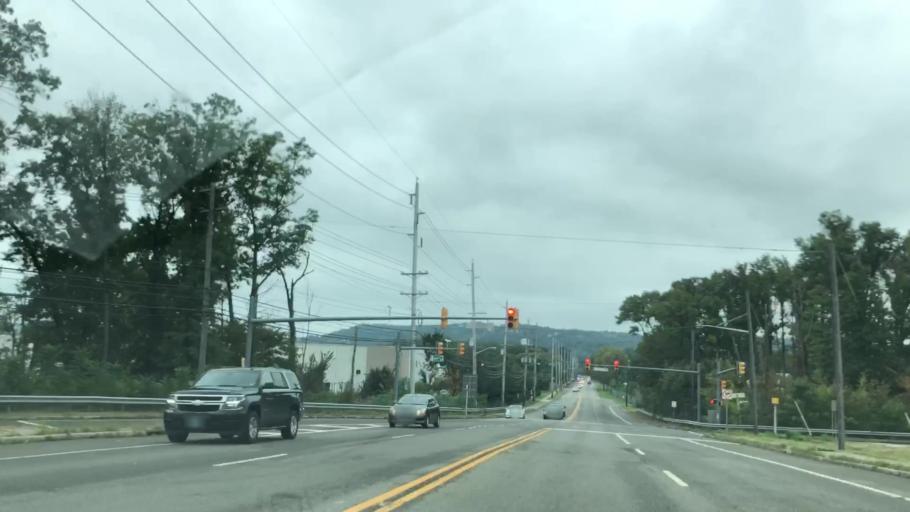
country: US
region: New Jersey
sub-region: Passaic County
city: Singac
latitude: 40.8926
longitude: -74.2264
